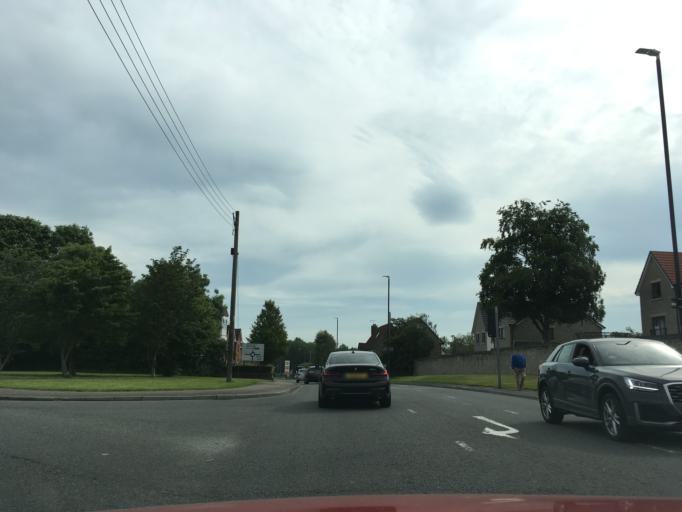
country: GB
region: England
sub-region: South Gloucestershire
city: Mangotsfield
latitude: 51.4953
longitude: -2.4856
